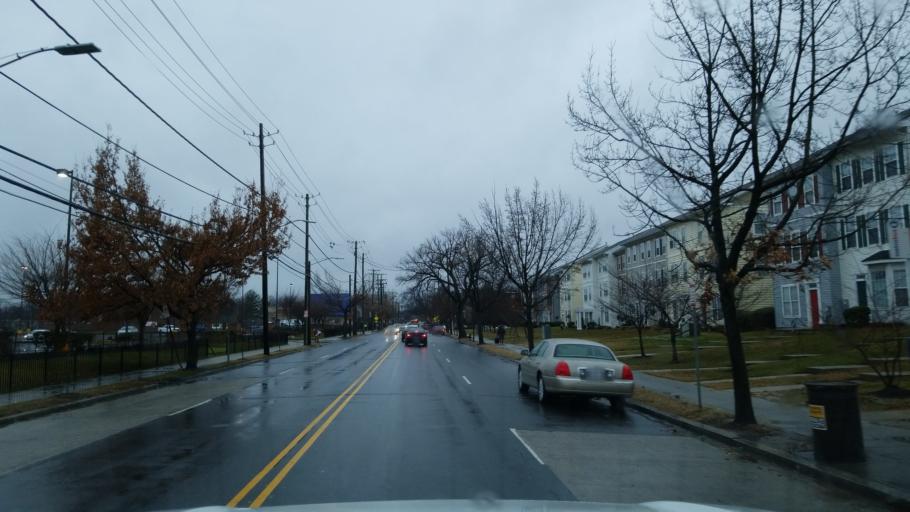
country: US
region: Maryland
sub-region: Prince George's County
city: Hillcrest Heights
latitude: 38.8468
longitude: -76.9808
